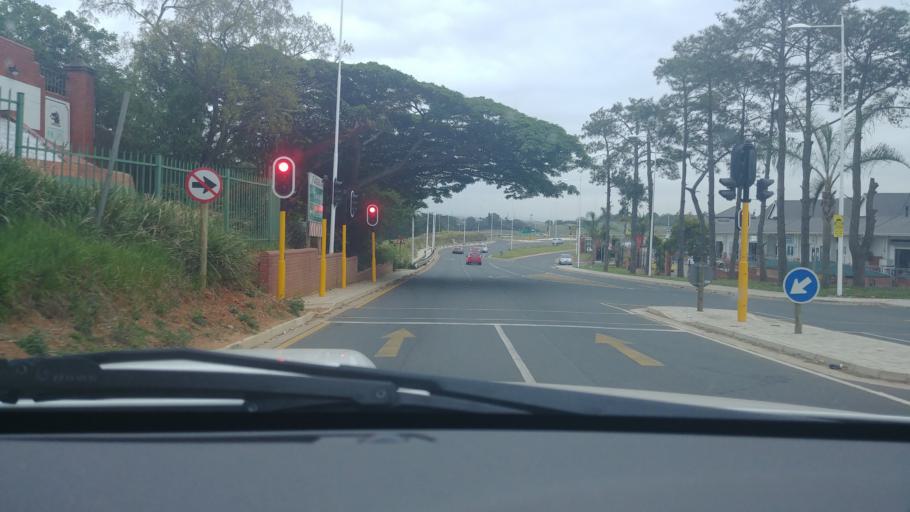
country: ZA
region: KwaZulu-Natal
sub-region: eThekwini Metropolitan Municipality
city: Durban
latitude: -29.7143
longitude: 31.0519
